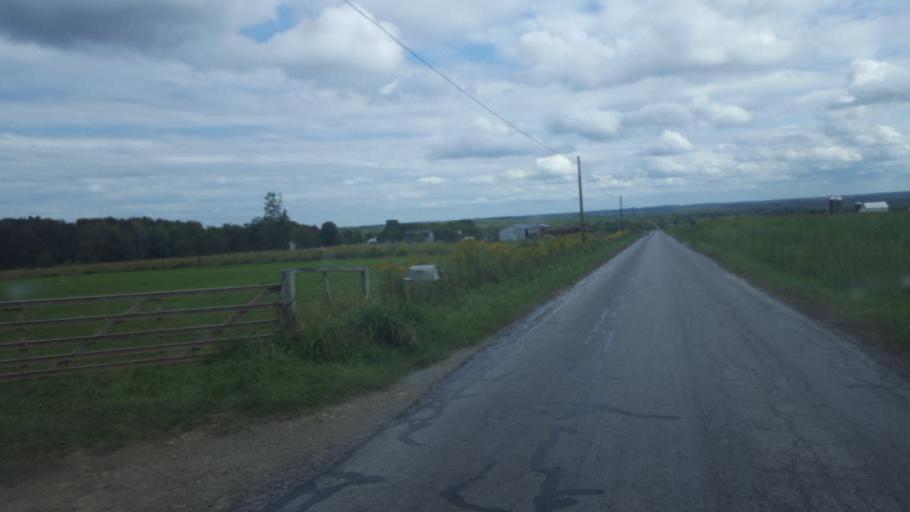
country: US
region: Pennsylvania
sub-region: Mercer County
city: Greenville
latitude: 41.4835
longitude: -80.2694
